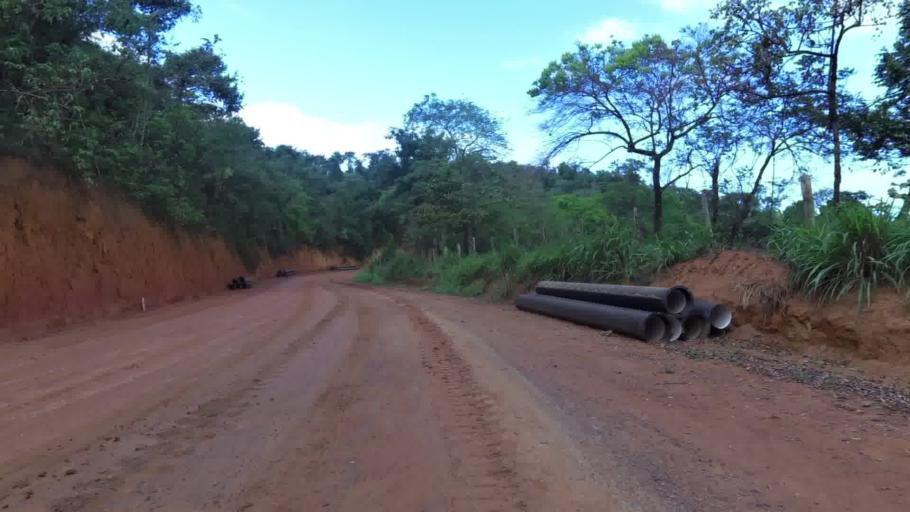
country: BR
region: Espirito Santo
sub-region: Piuma
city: Piuma
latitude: -20.8150
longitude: -40.6758
